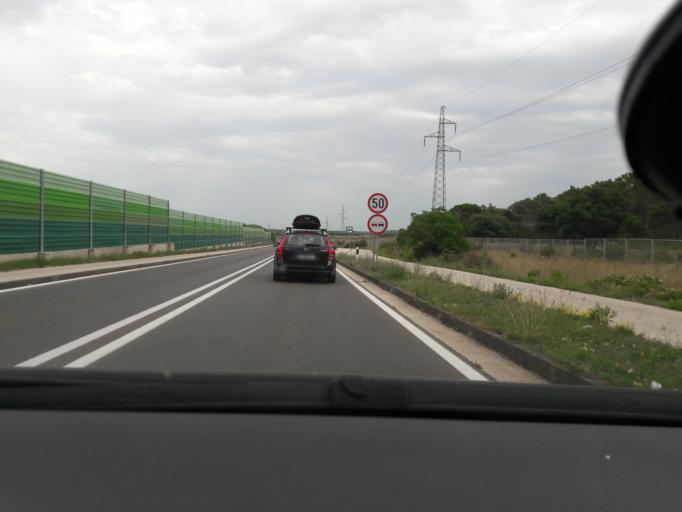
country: HR
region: Zadarska
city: Nin
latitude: 44.2369
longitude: 15.1755
